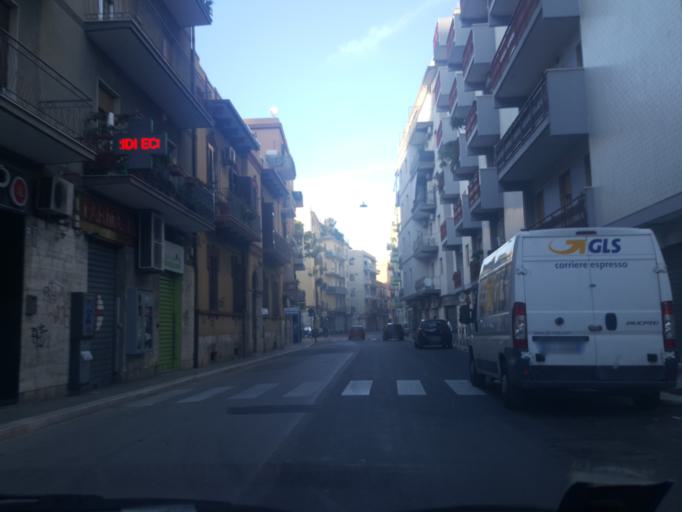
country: IT
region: Apulia
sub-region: Provincia di Bari
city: Bari
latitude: 41.1079
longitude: 16.8678
